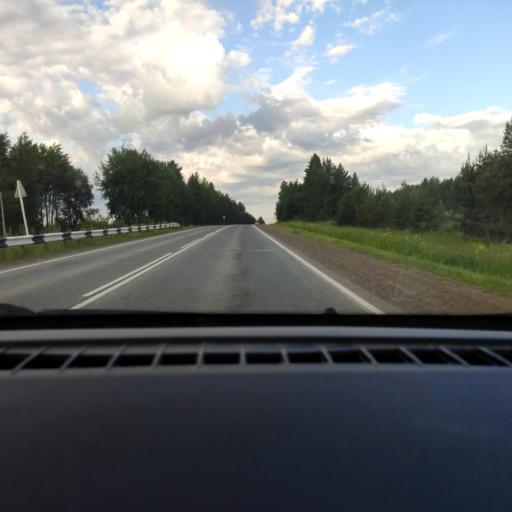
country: RU
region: Perm
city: Ocher
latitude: 57.4474
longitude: 54.4676
